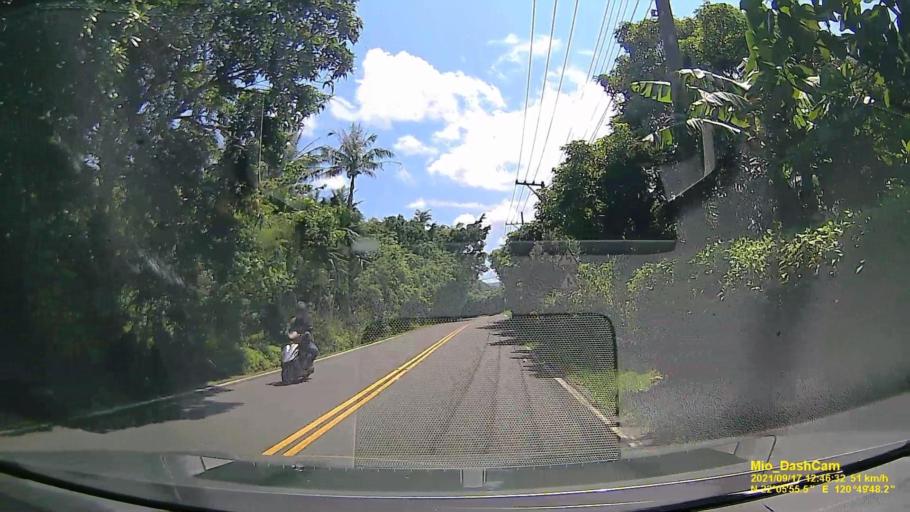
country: TW
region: Taiwan
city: Hengchun
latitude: 22.0986
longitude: 120.8300
